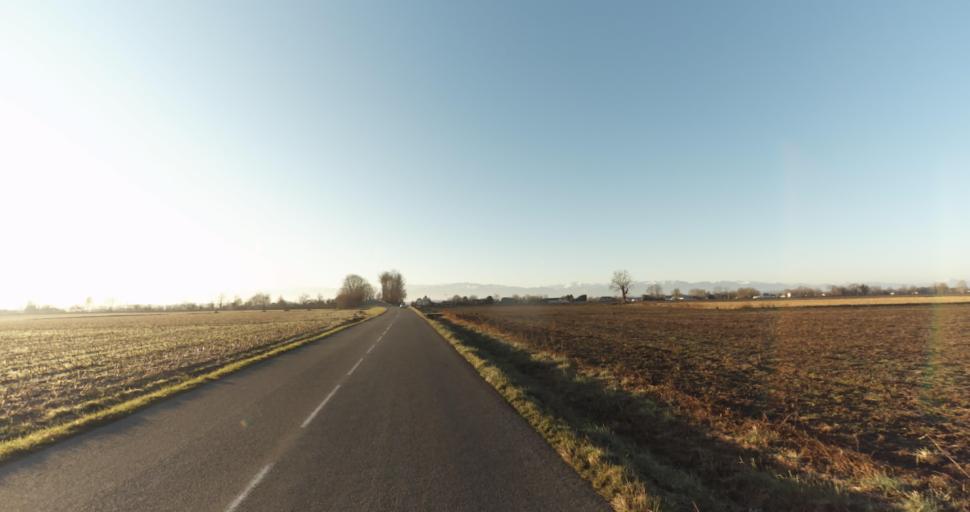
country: FR
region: Aquitaine
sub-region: Departement des Pyrenees-Atlantiques
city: Morlaas
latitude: 43.3189
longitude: -0.2750
